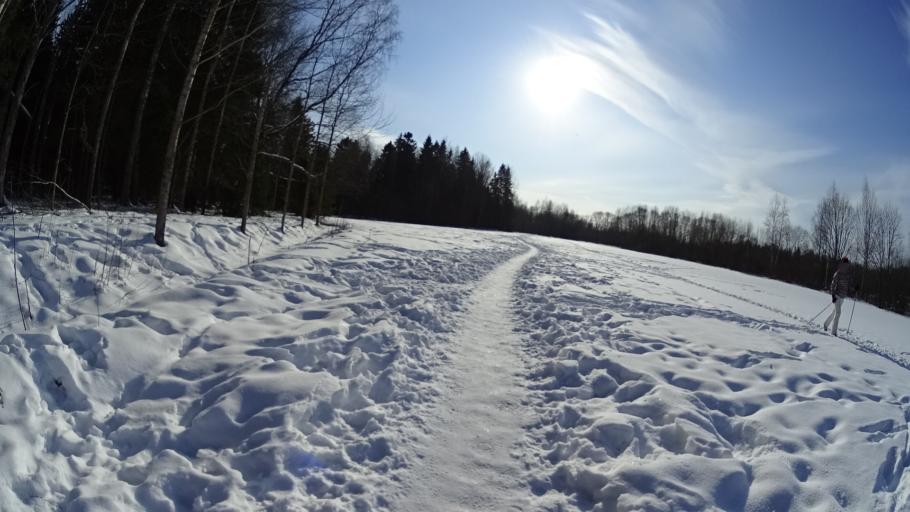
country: FI
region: Uusimaa
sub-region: Helsinki
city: Kauniainen
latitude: 60.2461
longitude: 24.7301
